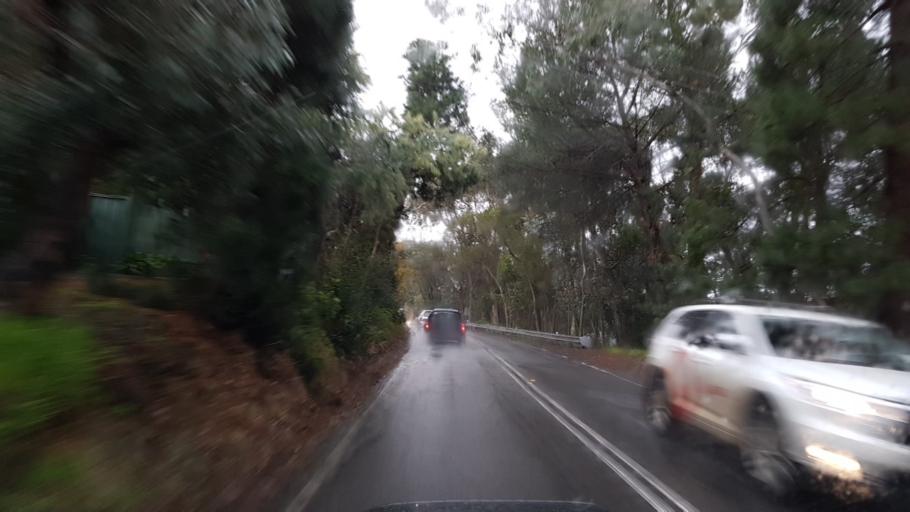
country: AU
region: South Australia
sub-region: Mitcham
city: Blackwood
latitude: -35.0264
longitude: 138.6241
